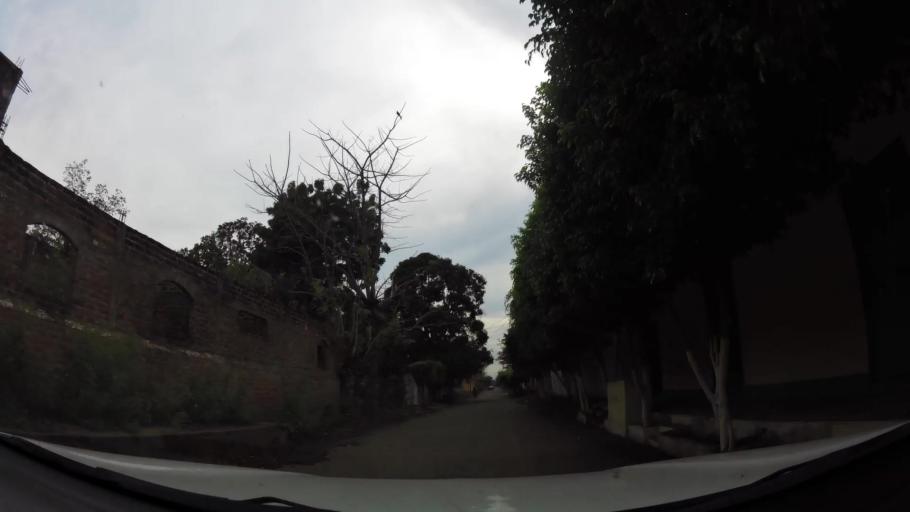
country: NI
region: Rivas
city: San Jorge
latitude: 11.4585
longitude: -85.8011
